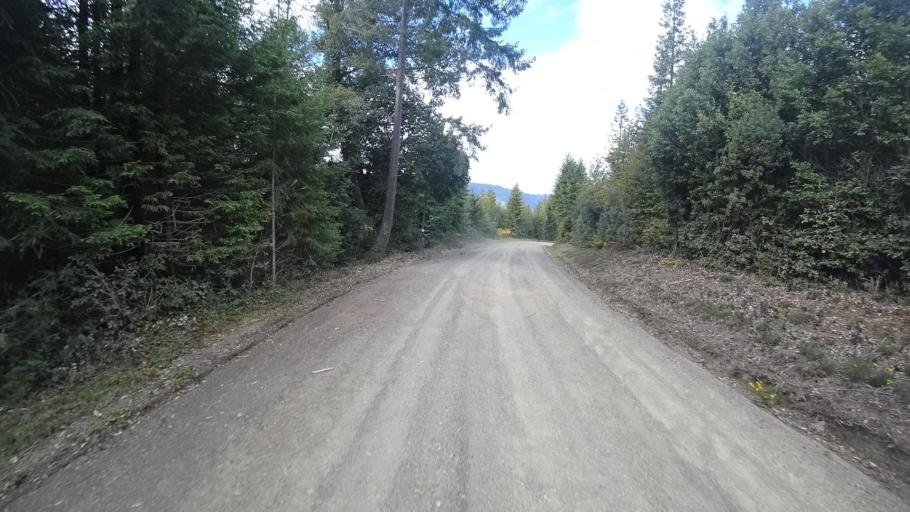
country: US
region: California
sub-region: Humboldt County
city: Blue Lake
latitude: 40.7707
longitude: -123.9587
